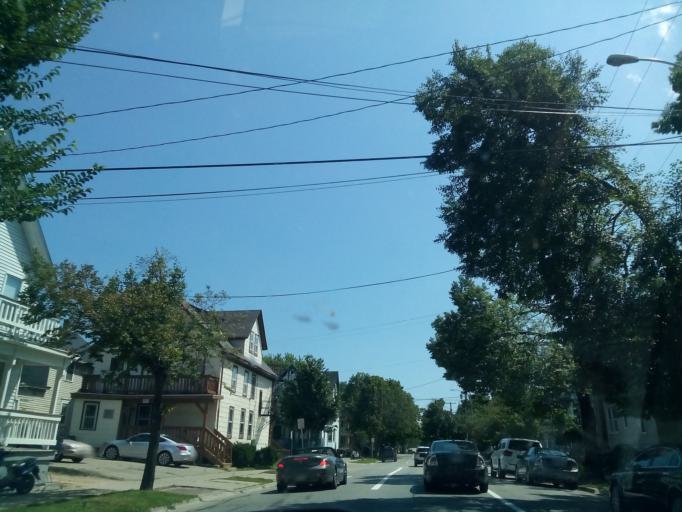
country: US
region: Wisconsin
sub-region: Dane County
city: Madison
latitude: 43.0714
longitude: -89.3923
